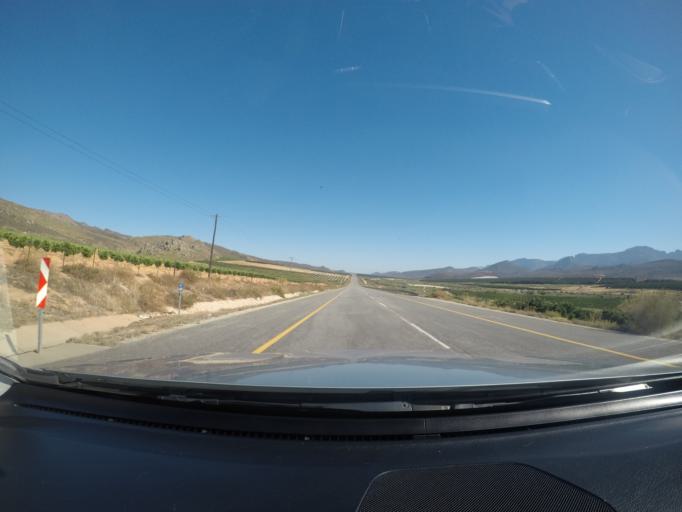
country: ZA
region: Western Cape
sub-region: West Coast District Municipality
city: Clanwilliam
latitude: -32.4971
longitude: 18.9663
